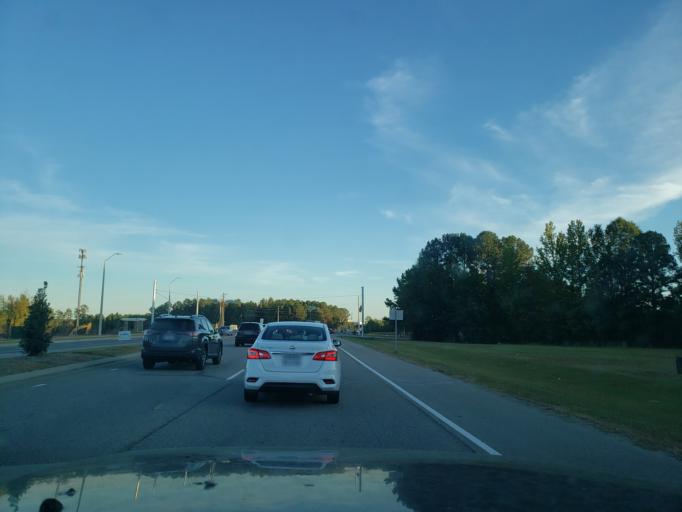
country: US
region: North Carolina
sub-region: Wake County
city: Morrisville
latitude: 35.8262
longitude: -78.8502
